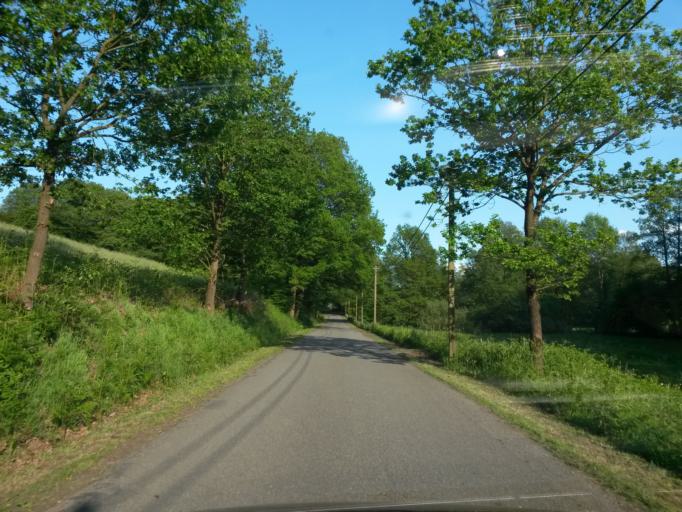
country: DE
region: North Rhine-Westphalia
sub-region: Regierungsbezirk Koln
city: Much
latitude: 50.8951
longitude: 7.3577
